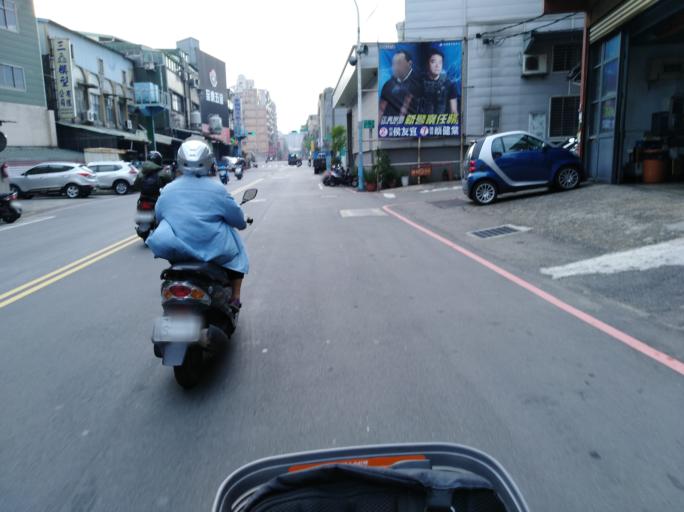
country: TW
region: Taipei
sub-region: Taipei
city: Banqiao
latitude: 25.0280
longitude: 121.4317
